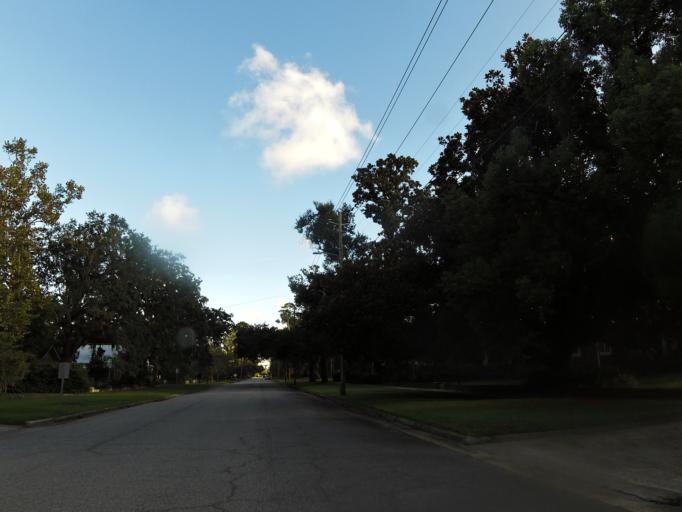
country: US
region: Georgia
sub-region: Glynn County
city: Brunswick
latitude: 31.1368
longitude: -81.4888
